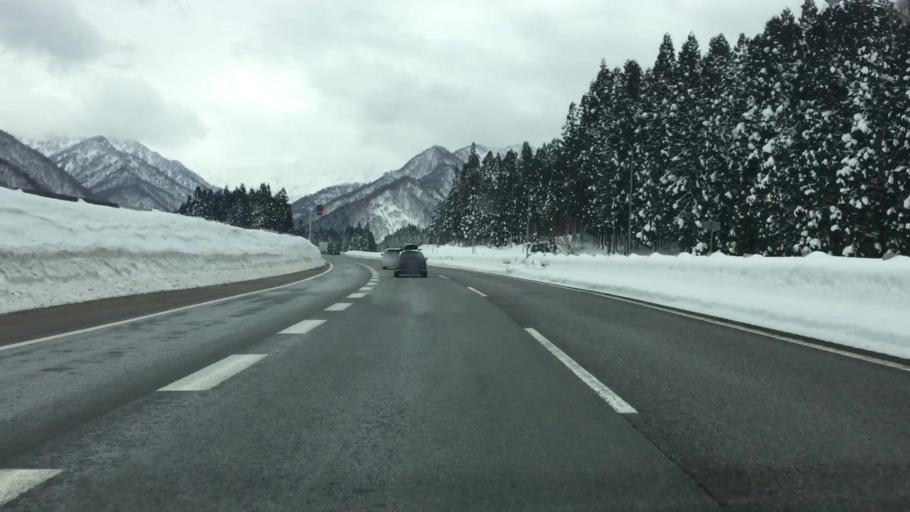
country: JP
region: Niigata
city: Shiozawa
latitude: 36.8933
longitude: 138.8459
